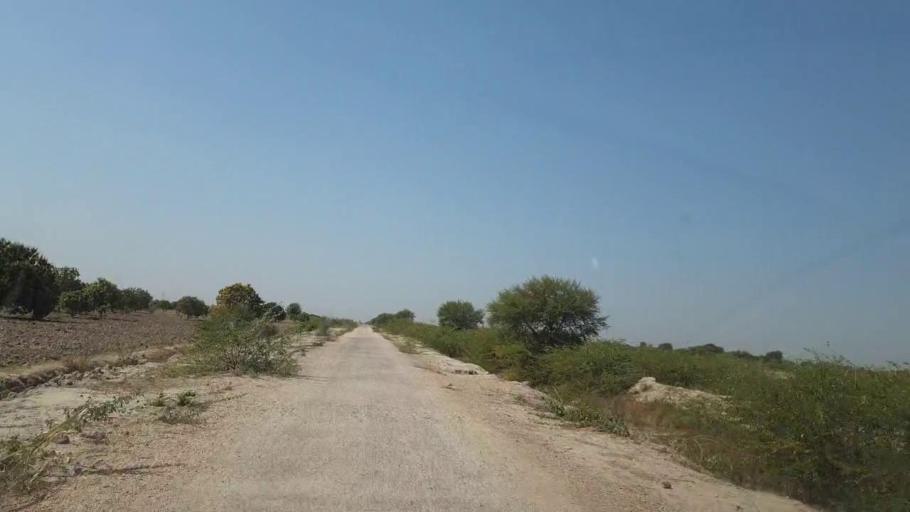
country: PK
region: Sindh
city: Kunri
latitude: 25.0963
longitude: 69.5200
